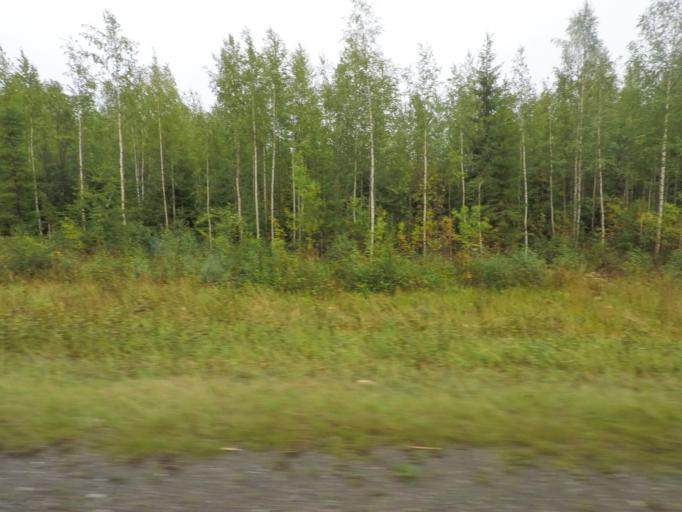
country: FI
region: Southern Savonia
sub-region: Pieksaemaeki
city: Joroinen
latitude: 62.1175
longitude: 27.8379
